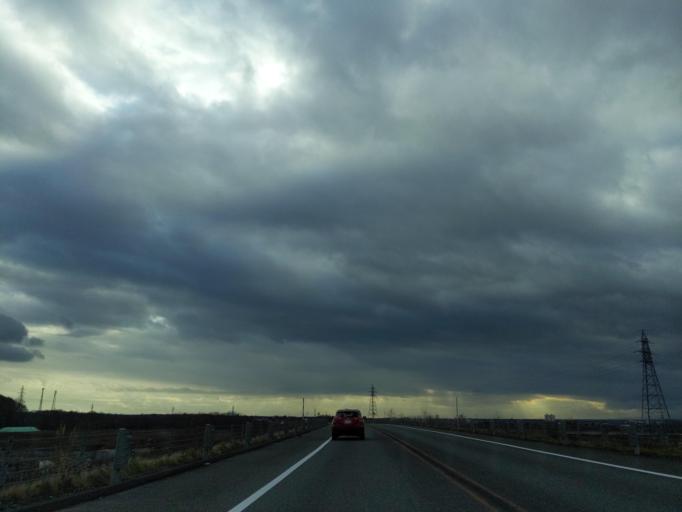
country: JP
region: Hokkaido
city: Chitose
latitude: 42.8417
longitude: 141.6942
